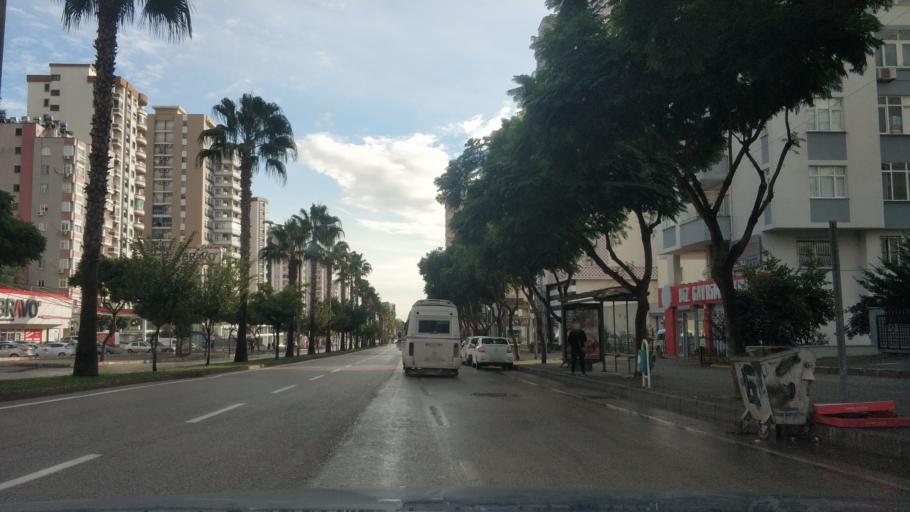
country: TR
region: Adana
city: Seyhan
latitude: 37.0468
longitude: 35.2716
